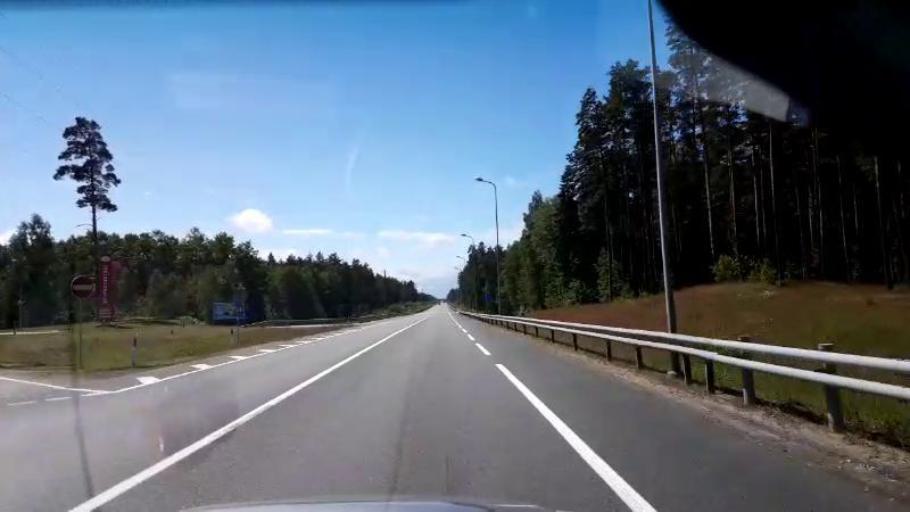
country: LV
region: Saulkrastu
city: Saulkrasti
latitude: 57.2257
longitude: 24.4164
